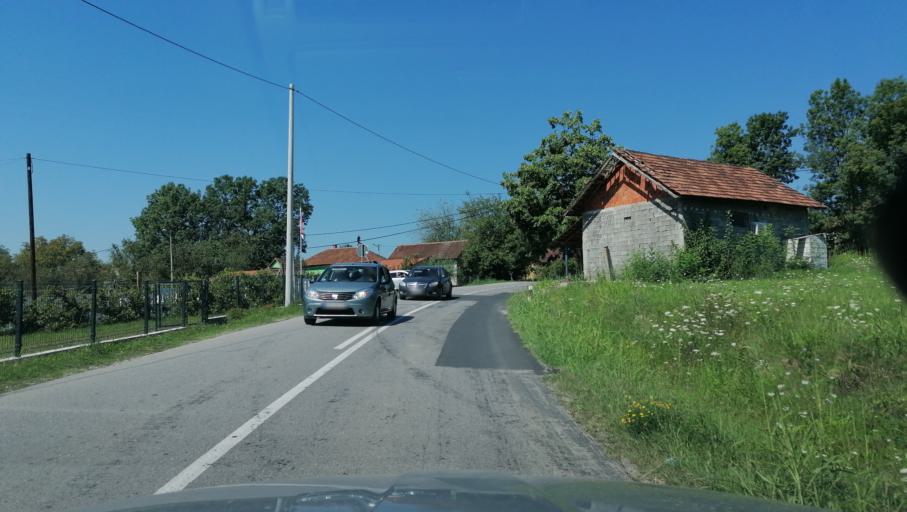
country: RS
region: Central Serbia
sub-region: Raski Okrug
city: Kraljevo
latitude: 43.7173
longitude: 20.8069
